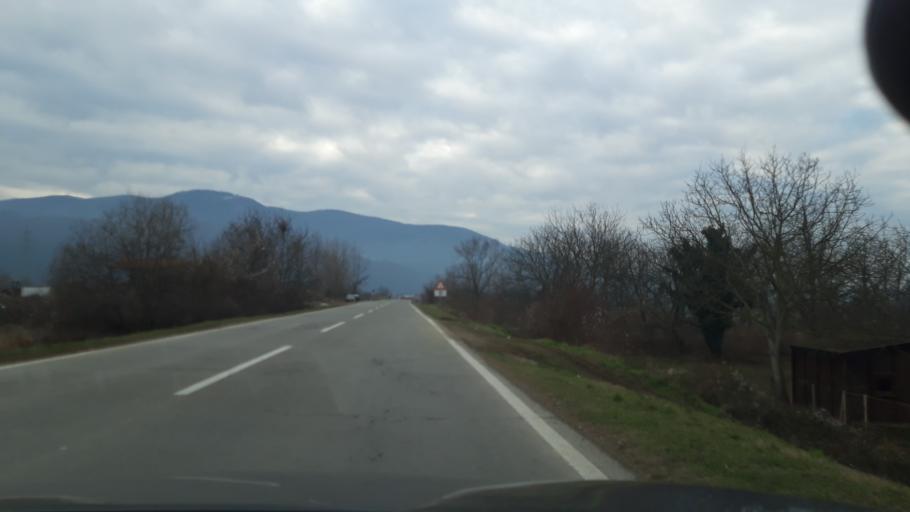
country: RS
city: Trsic
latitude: 44.5320
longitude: 19.1807
